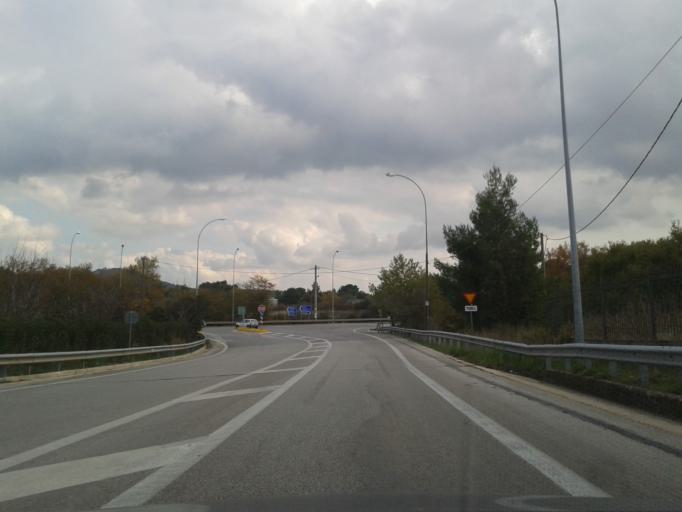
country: GR
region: Attica
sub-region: Nomarchia Anatolikis Attikis
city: Afidnes
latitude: 38.1886
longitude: 23.8535
